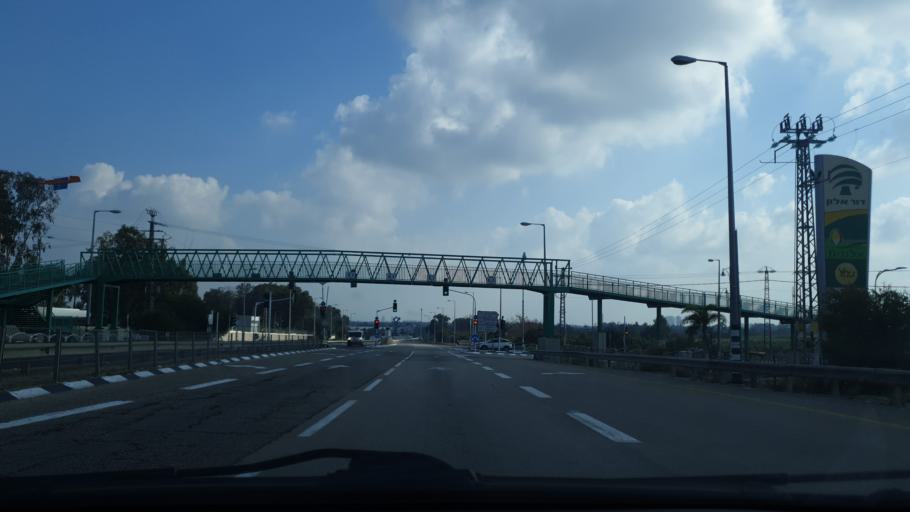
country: IL
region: Central District
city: Kefar Habad
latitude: 31.9698
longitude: 34.8432
